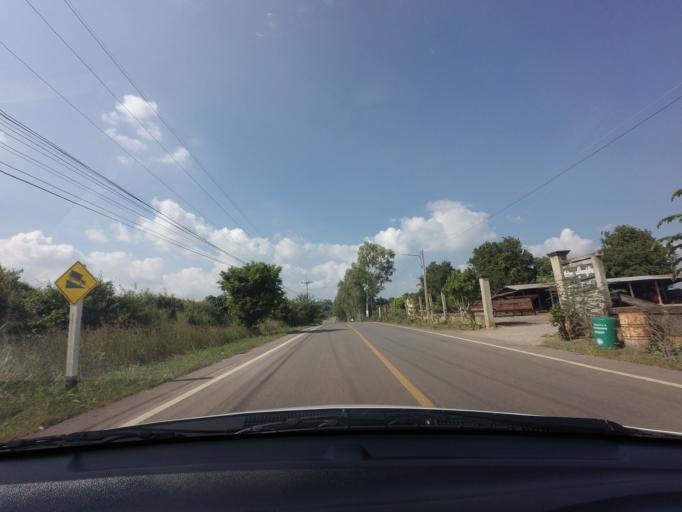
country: TH
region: Nakhon Ratchasima
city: Wang Nam Khiao
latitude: 14.4748
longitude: 101.6246
